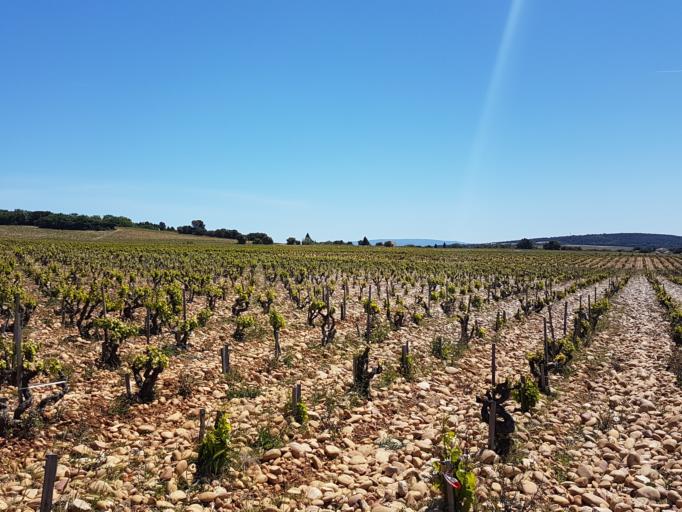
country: FR
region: Provence-Alpes-Cote d'Azur
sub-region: Departement du Vaucluse
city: Bedarrides
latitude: 44.0388
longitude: 4.8702
